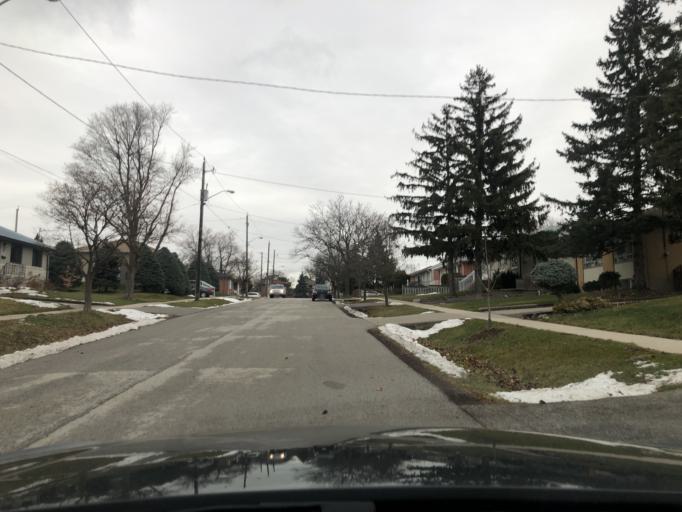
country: CA
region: Ontario
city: Etobicoke
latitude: 43.6979
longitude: -79.5366
